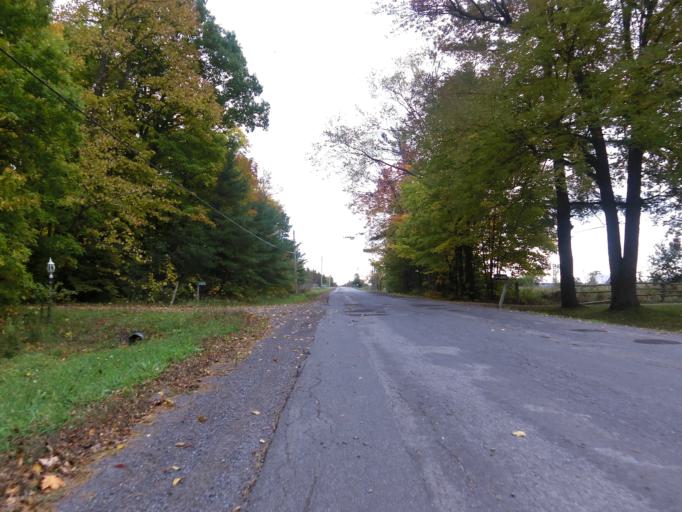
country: CA
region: Ontario
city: Arnprior
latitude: 45.4712
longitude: -76.1558
